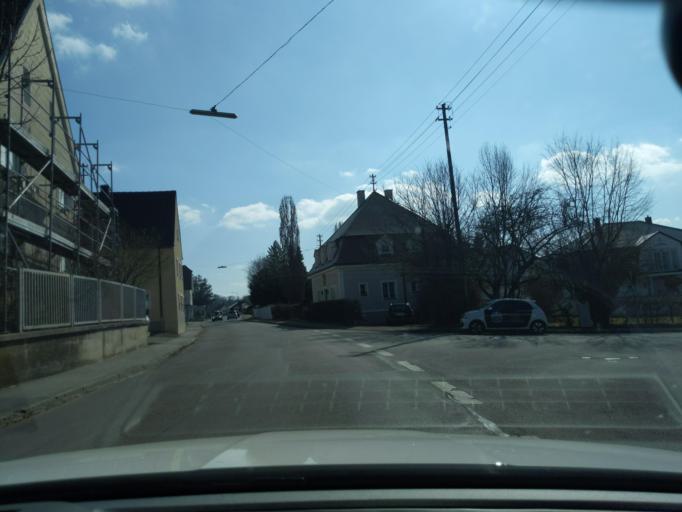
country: DE
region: Bavaria
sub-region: Swabia
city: Buch
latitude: 48.2352
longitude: 10.1762
